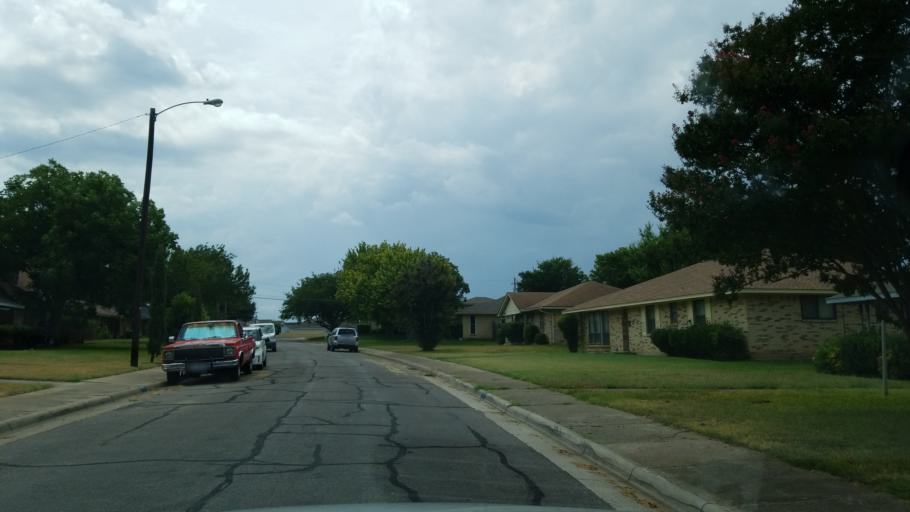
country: US
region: Texas
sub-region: Dallas County
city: Duncanville
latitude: 32.6589
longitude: -96.8528
